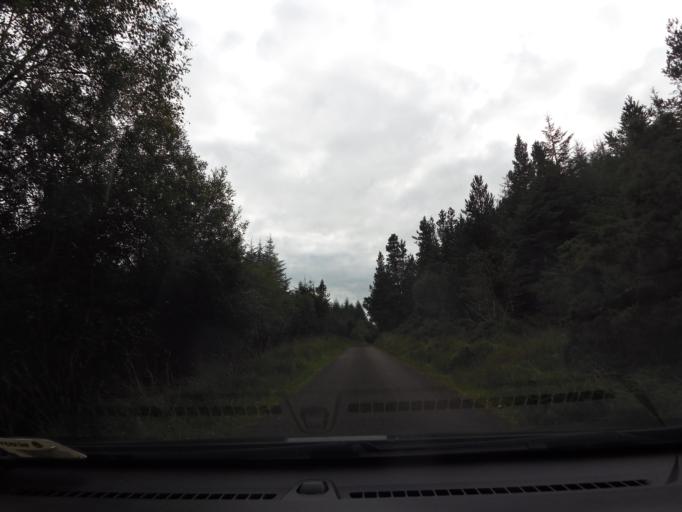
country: IE
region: Connaught
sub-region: County Galway
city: Loughrea
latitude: 53.1336
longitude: -8.5007
